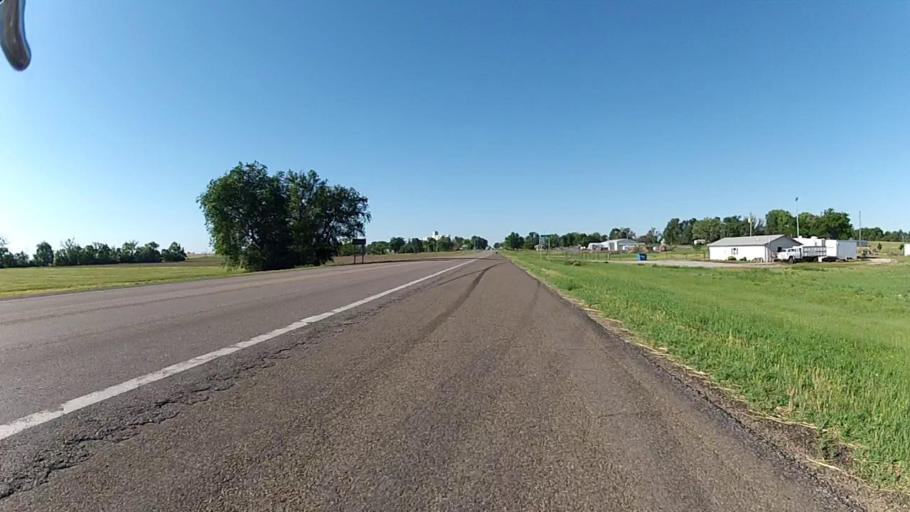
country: US
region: Kansas
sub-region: Ford County
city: Dodge City
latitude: 37.6436
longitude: -99.7538
